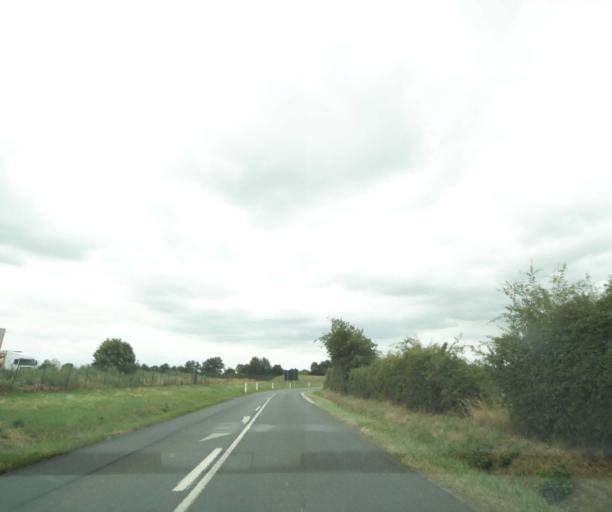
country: FR
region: Pays de la Loire
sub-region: Departement de la Sarthe
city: Sable-sur-Sarthe
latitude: 47.8245
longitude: -0.3184
